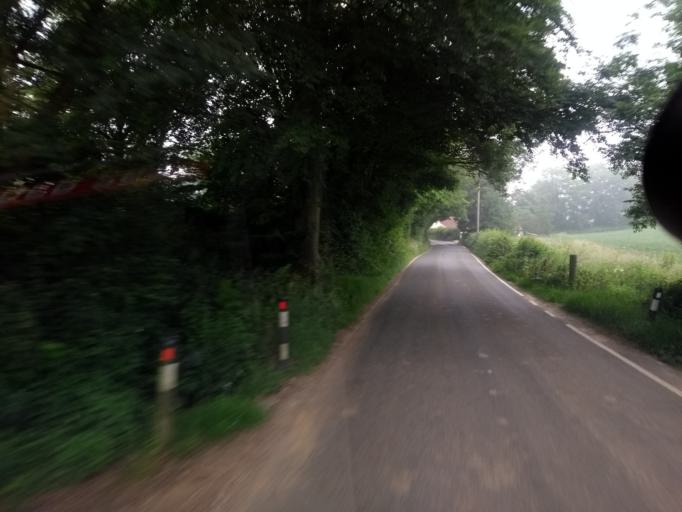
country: GB
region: England
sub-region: Somerset
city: Crewkerne
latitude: 50.8286
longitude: -2.8083
